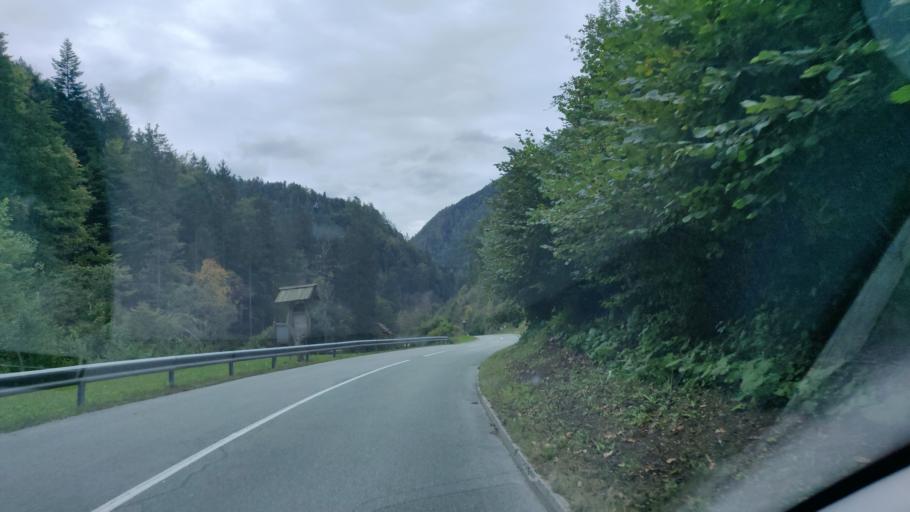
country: SI
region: Jezersko
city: Zgornje Jezersko
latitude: 46.3636
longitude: 14.4698
